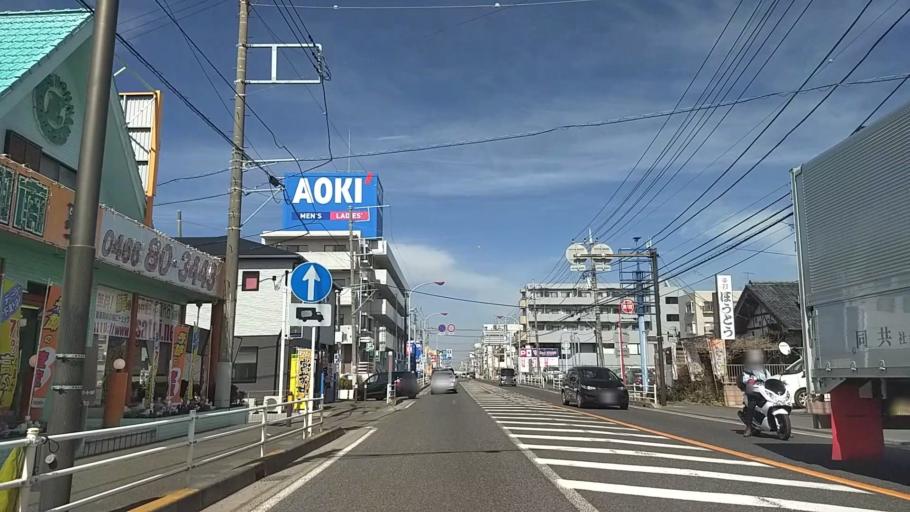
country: JP
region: Kanagawa
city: Fujisawa
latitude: 35.3794
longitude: 139.4762
